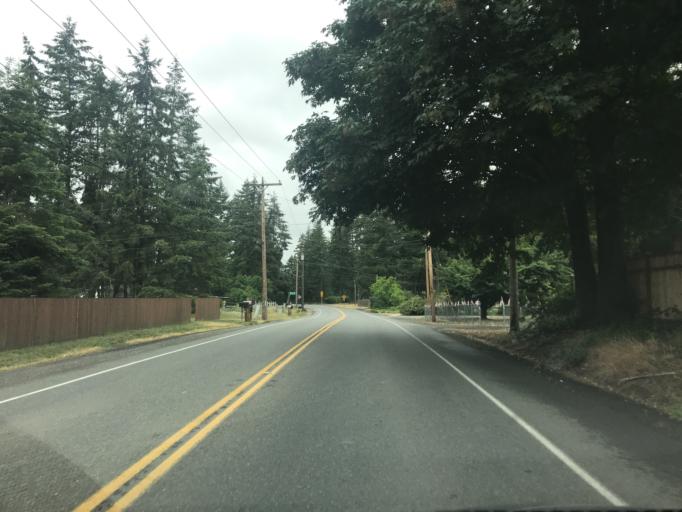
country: US
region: Washington
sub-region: King County
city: Lake Morton-Berrydale
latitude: 47.3417
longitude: -122.0943
